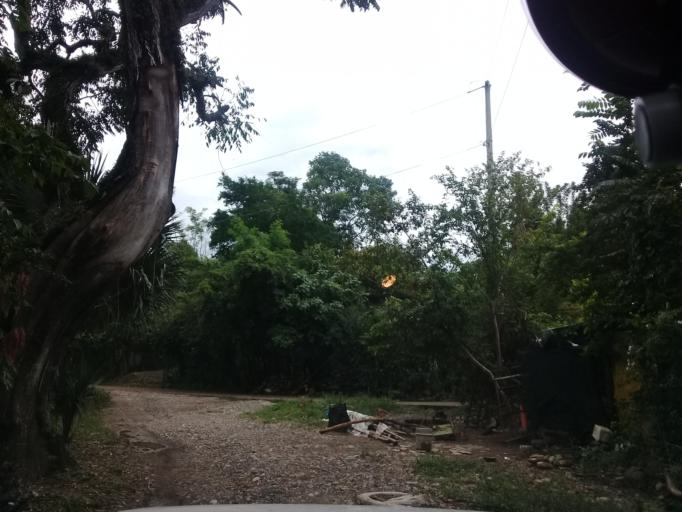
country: MX
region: Veracruz
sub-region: Chalma
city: San Pedro Coyutla
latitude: 21.2055
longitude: -98.3956
